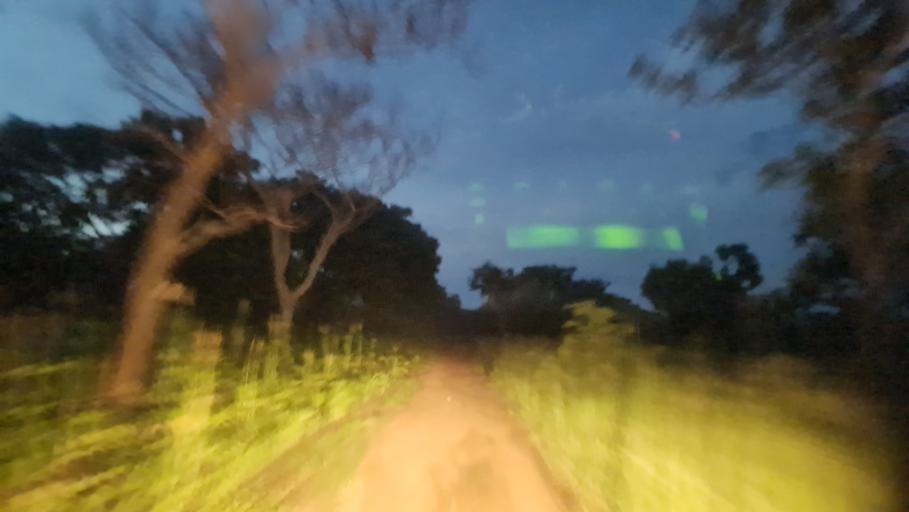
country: MZ
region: Nampula
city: Nampula
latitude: -14.6779
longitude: 39.8315
